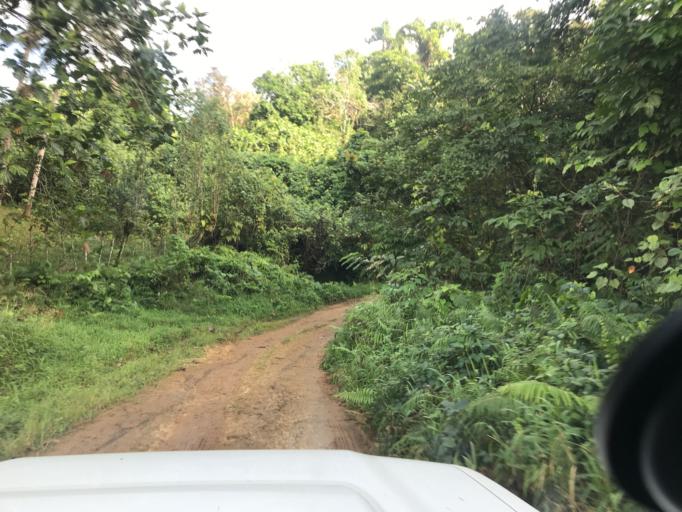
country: VU
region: Sanma
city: Luganville
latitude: -15.4609
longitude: 167.0730
